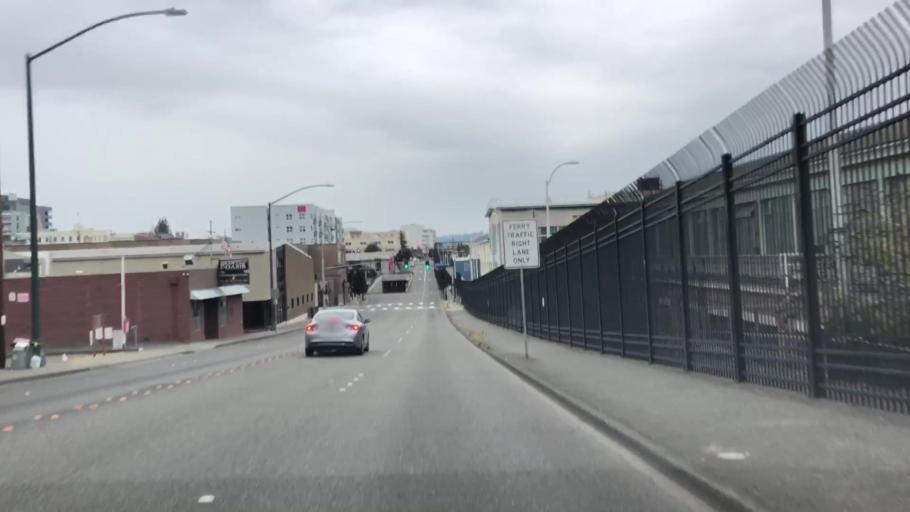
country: US
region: Washington
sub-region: Kitsap County
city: Bremerton
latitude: 47.5650
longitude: -122.6319
